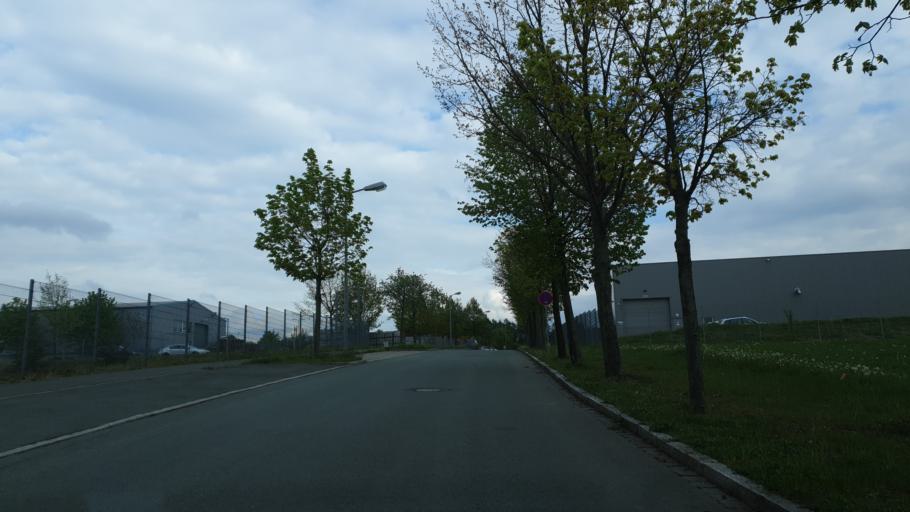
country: DE
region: Saxony
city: Oelsnitz
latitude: 50.7165
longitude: 12.7145
